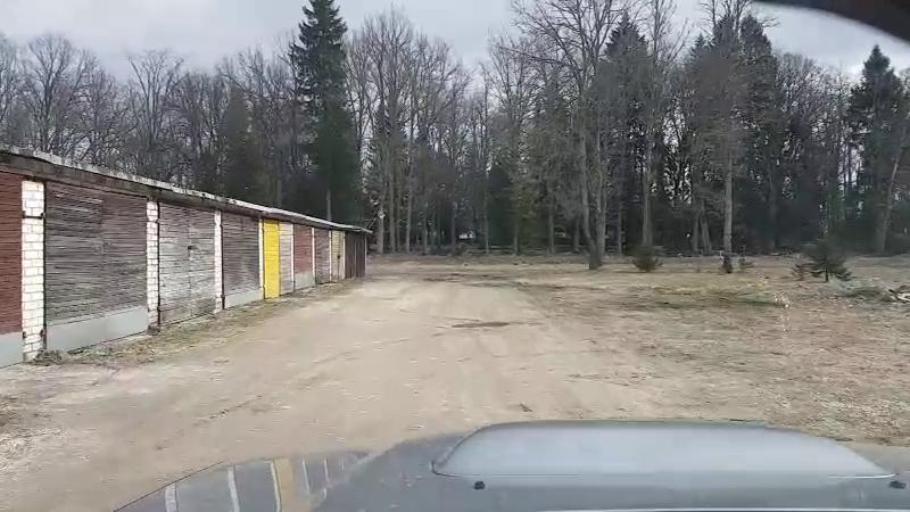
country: EE
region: Jaervamaa
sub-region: Paide linn
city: Paide
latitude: 58.8828
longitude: 25.5341
